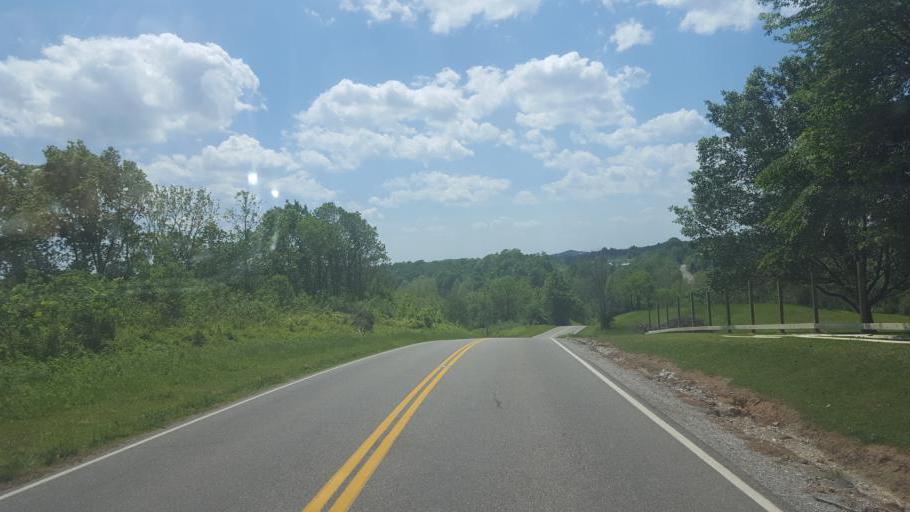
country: US
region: Ohio
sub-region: Jackson County
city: Oak Hill
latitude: 38.8186
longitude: -82.4010
